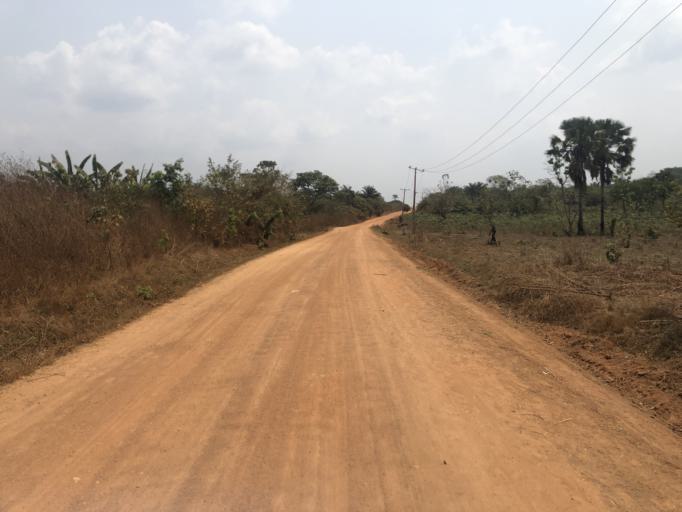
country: NG
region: Osun
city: Bode Osi
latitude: 7.7859
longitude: 4.1909
